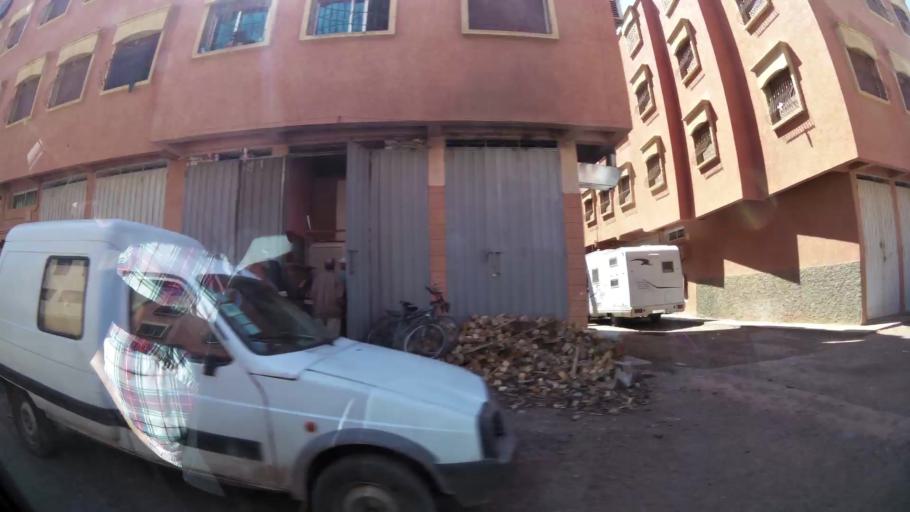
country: MA
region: Souss-Massa-Draa
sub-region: Inezgane-Ait Mellou
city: Inezgane
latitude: 30.3378
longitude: -9.5085
